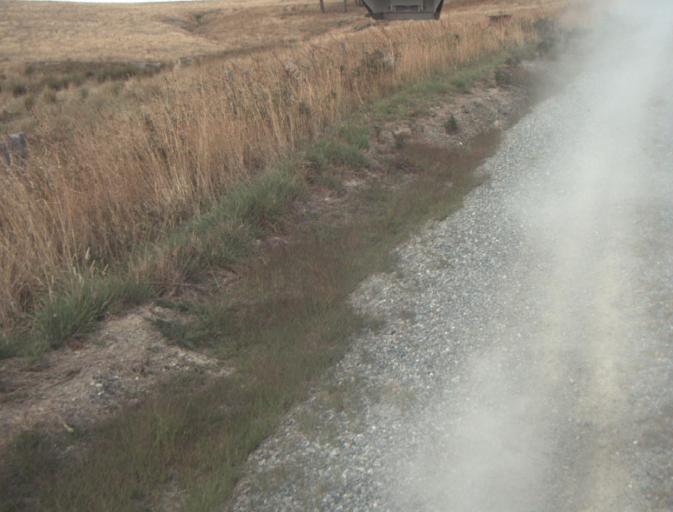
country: AU
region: Tasmania
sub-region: Launceston
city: Mayfield
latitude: -41.2137
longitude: 147.1081
